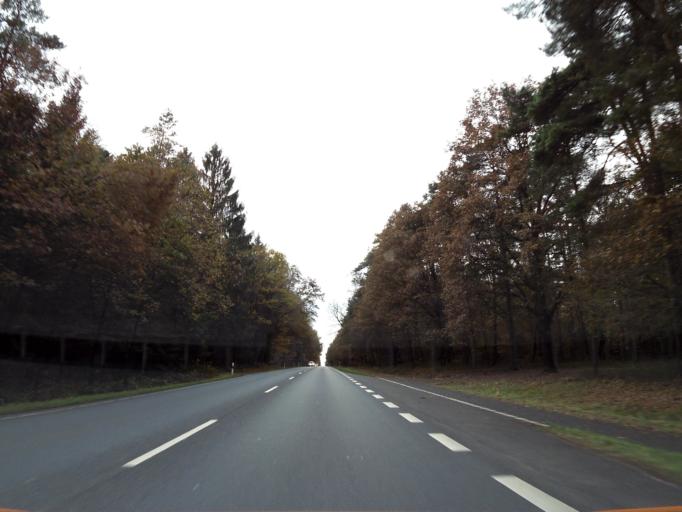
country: DE
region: Lower Saxony
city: Bispingen
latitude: 53.0071
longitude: 9.9477
